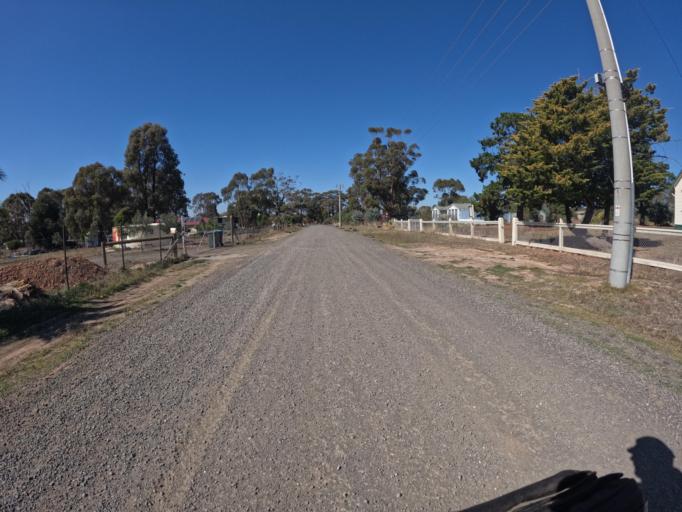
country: AU
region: Victoria
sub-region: Greater Bendigo
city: Kennington
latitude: -36.8274
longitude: 144.5853
